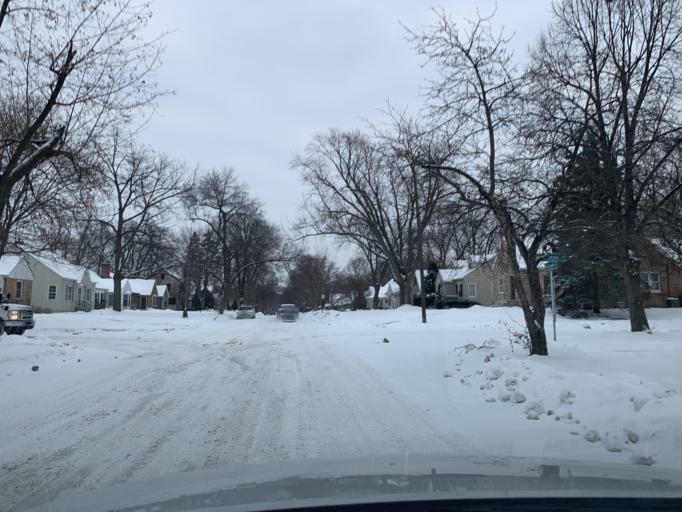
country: US
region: Minnesota
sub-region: Hennepin County
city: Saint Louis Park
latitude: 44.9316
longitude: -93.3424
